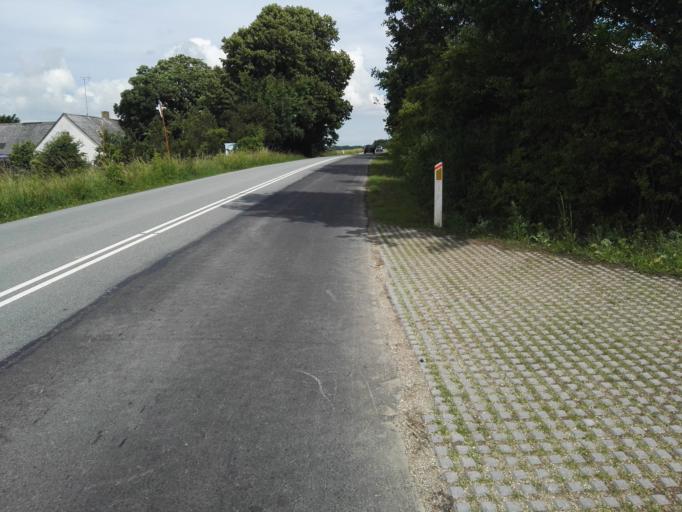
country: DK
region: Capital Region
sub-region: Frederikssund Kommune
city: Slangerup
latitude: 55.8588
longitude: 12.1741
